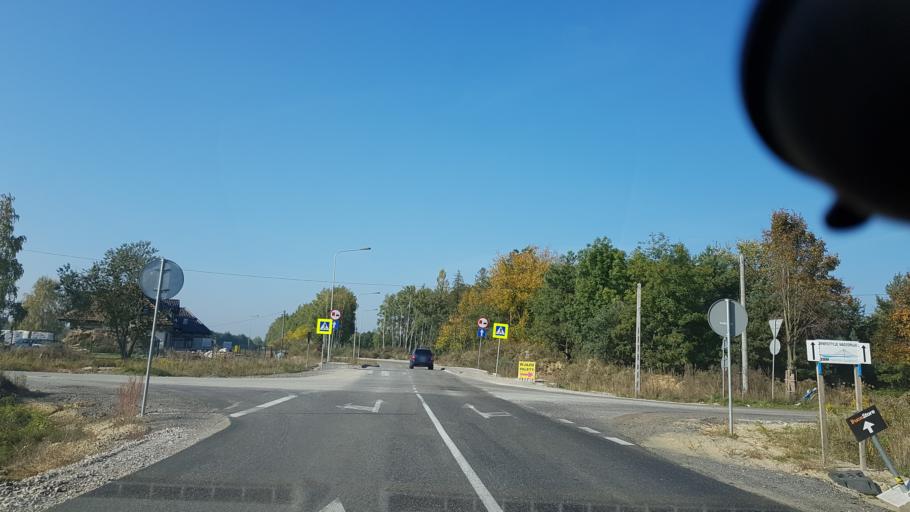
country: PL
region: Masovian Voivodeship
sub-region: Powiat pruszkowski
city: Nadarzyn
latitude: 52.0770
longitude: 20.7721
